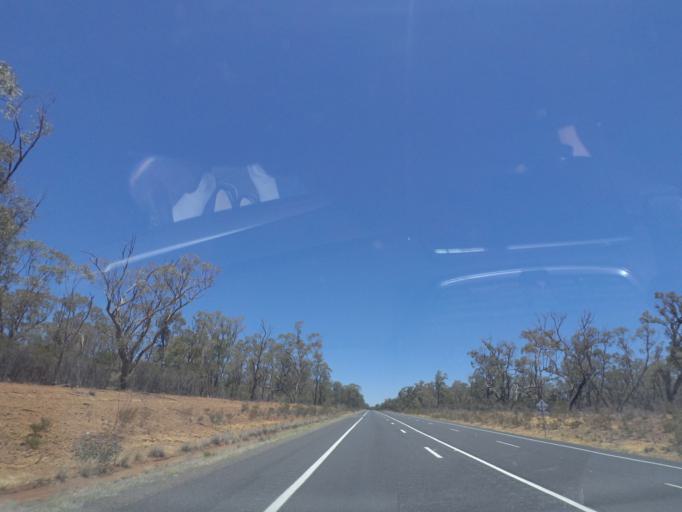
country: AU
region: New South Wales
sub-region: Warrumbungle Shire
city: Coonabarabran
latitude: -30.8725
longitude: 149.4496
